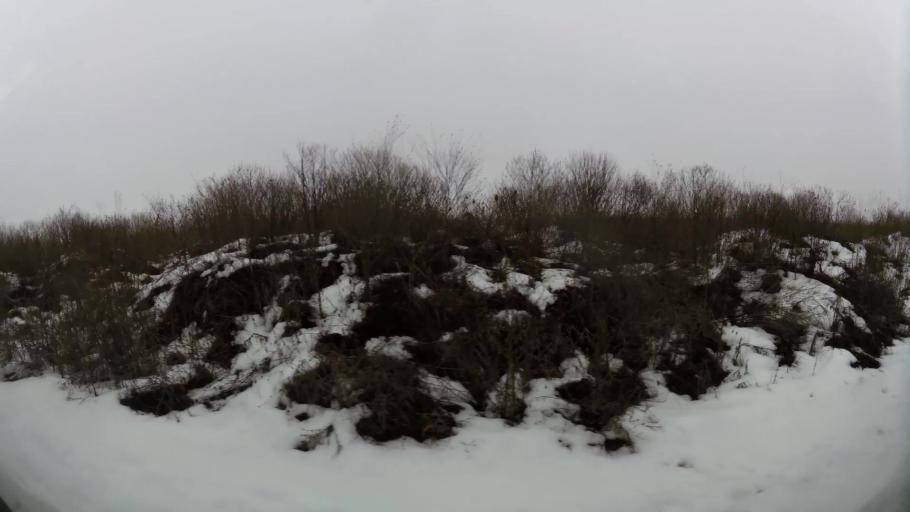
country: RO
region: Ilfov
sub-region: Comuna Chiajna
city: Chiajna
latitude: 44.4475
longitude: 25.9661
